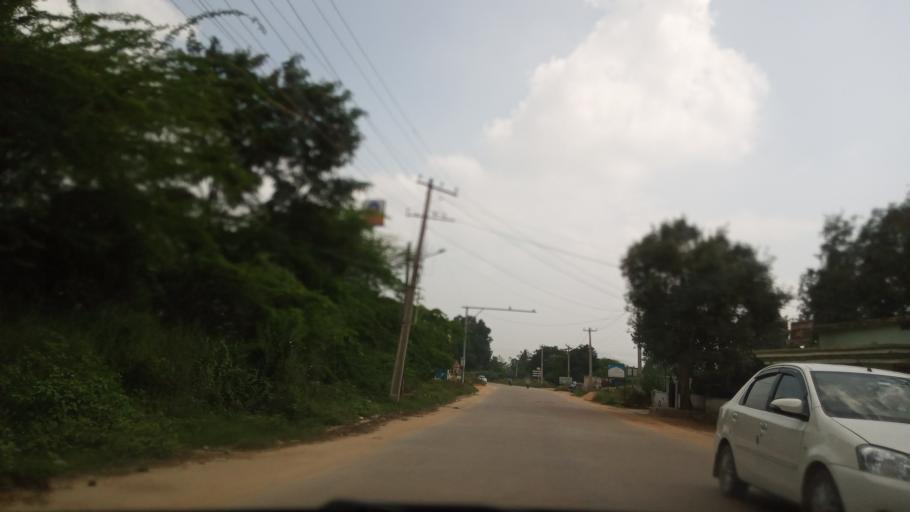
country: IN
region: Andhra Pradesh
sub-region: Chittoor
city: Madanapalle
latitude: 13.6380
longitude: 78.6361
